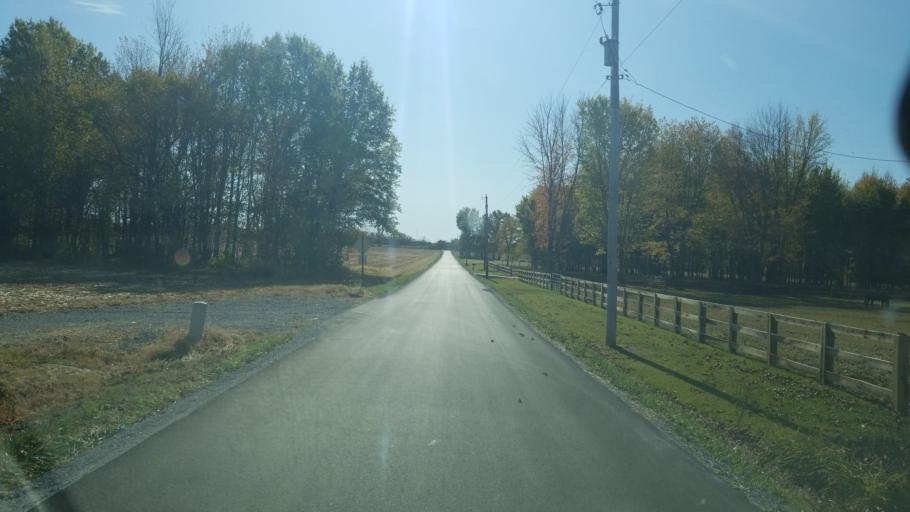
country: US
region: Ohio
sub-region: Warren County
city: Morrow
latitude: 39.3869
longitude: -84.0464
